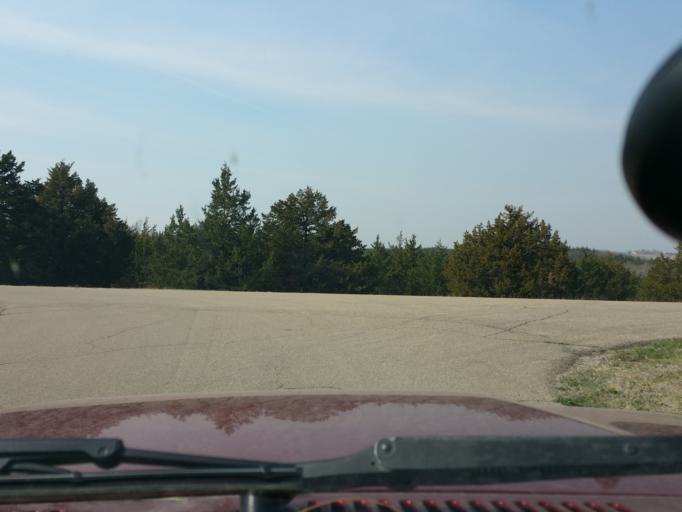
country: US
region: Kansas
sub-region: Marshall County
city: Blue Rapids
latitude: 39.4434
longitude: -96.7358
